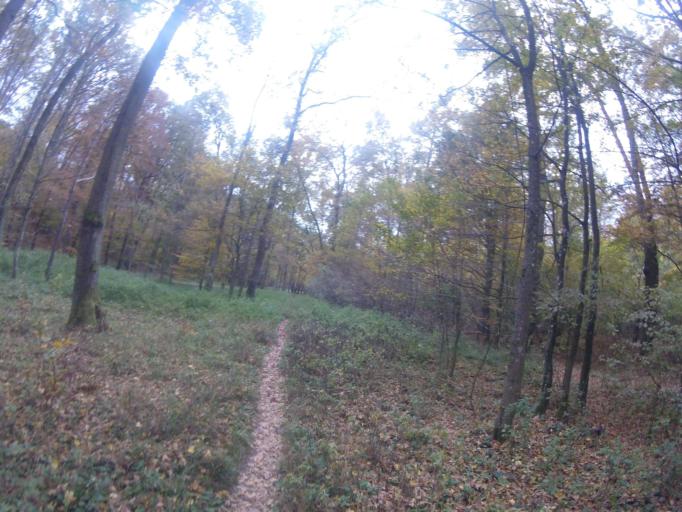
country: HU
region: Veszprem
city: Herend
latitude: 47.2585
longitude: 17.7417
